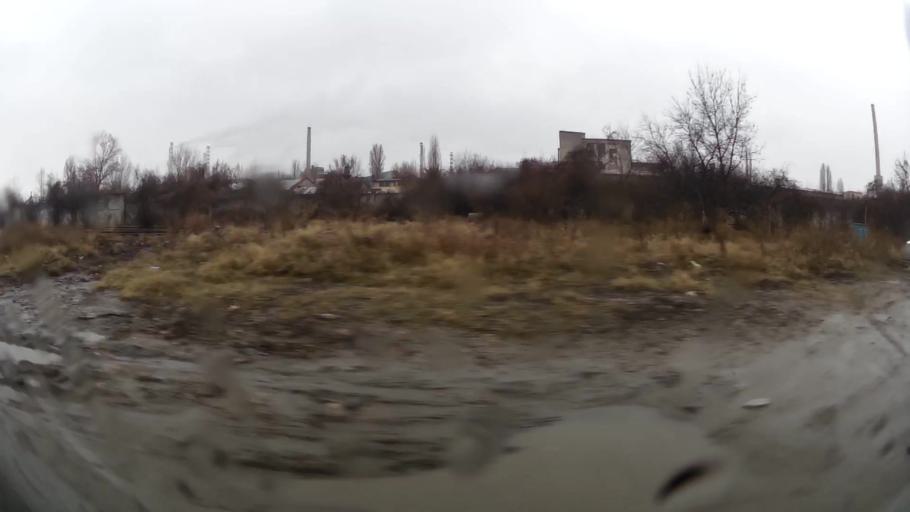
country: BG
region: Sofia-Capital
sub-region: Stolichna Obshtina
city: Sofia
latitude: 42.6611
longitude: 23.4204
